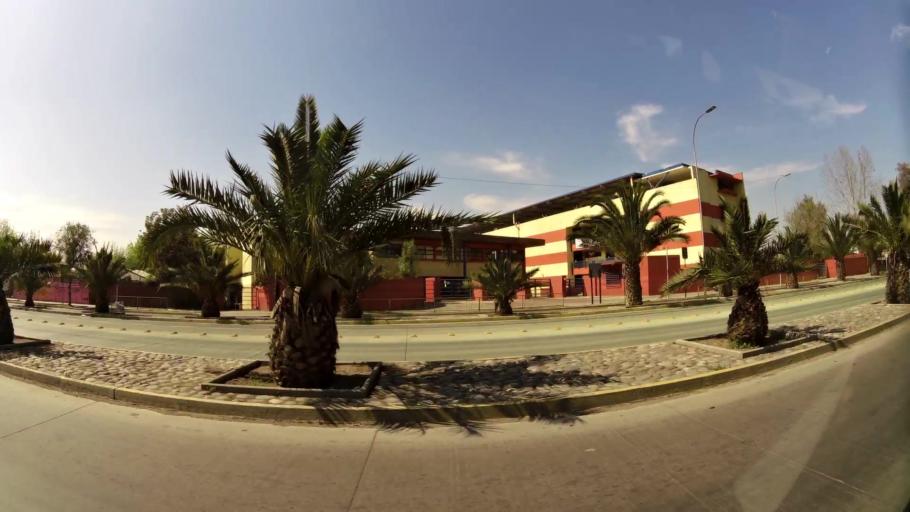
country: CL
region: Santiago Metropolitan
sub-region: Provincia de Santiago
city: Lo Prado
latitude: -33.4040
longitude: -70.7033
